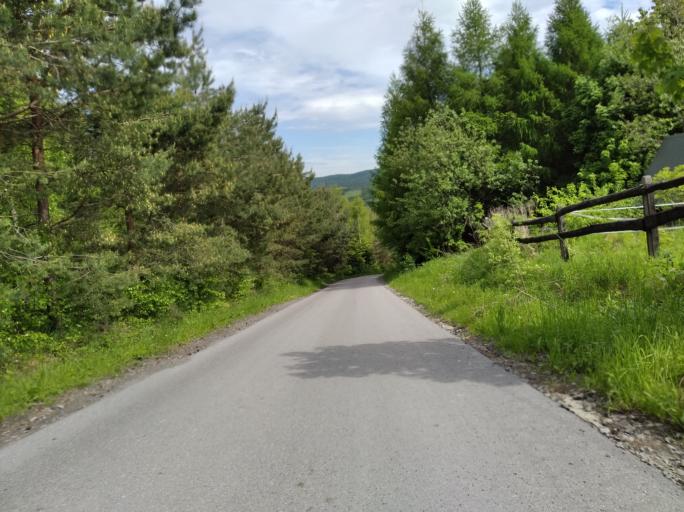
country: PL
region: Subcarpathian Voivodeship
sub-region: Powiat strzyzowski
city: Frysztak
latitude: 49.8382
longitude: 21.5233
